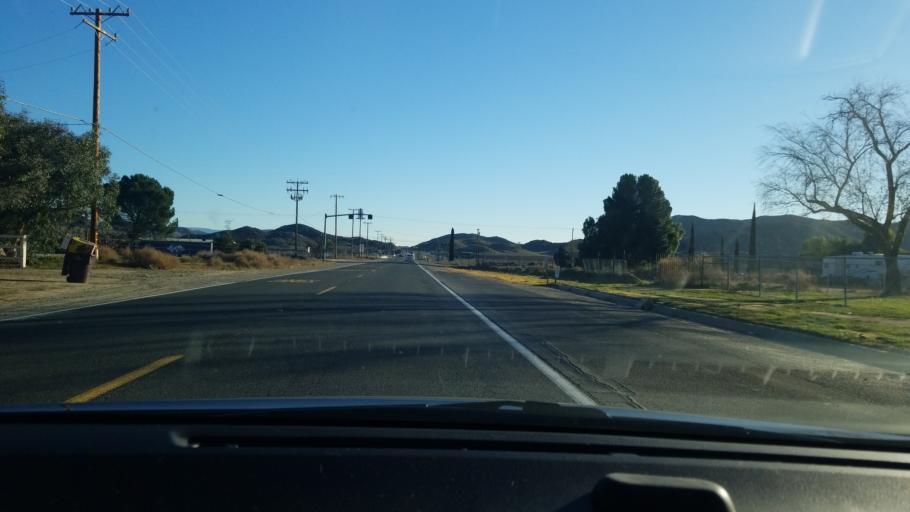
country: US
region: California
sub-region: Riverside County
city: Winchester
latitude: 33.7020
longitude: -117.0849
